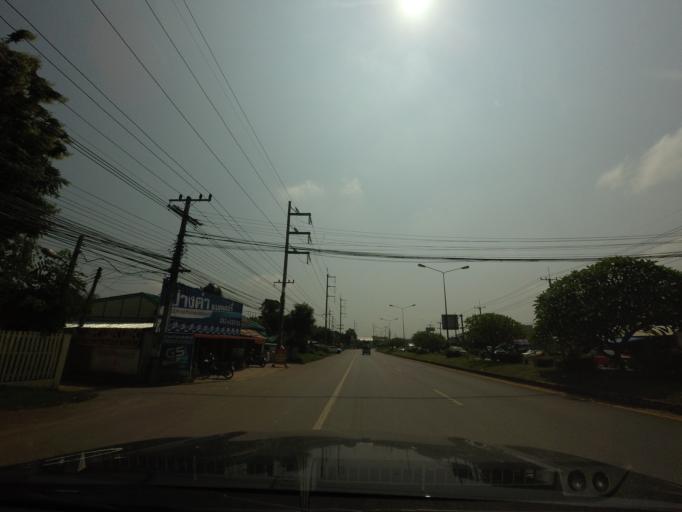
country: TH
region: Nan
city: Nan
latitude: 18.7864
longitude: 100.7430
